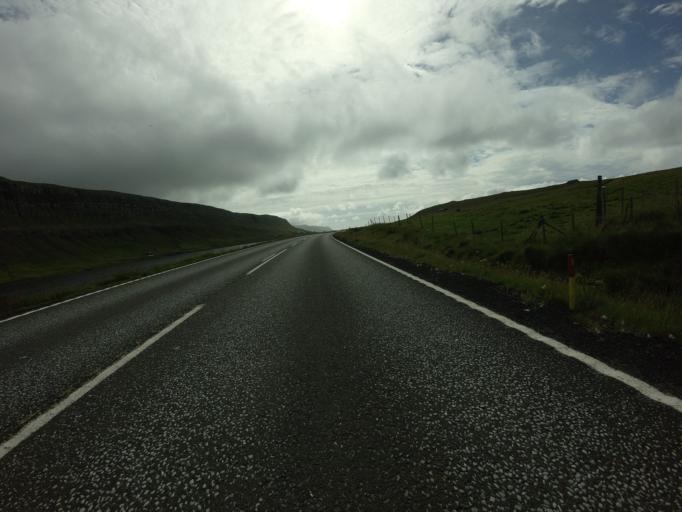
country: FO
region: Sandoy
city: Sandur
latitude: 61.8542
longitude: -6.8274
